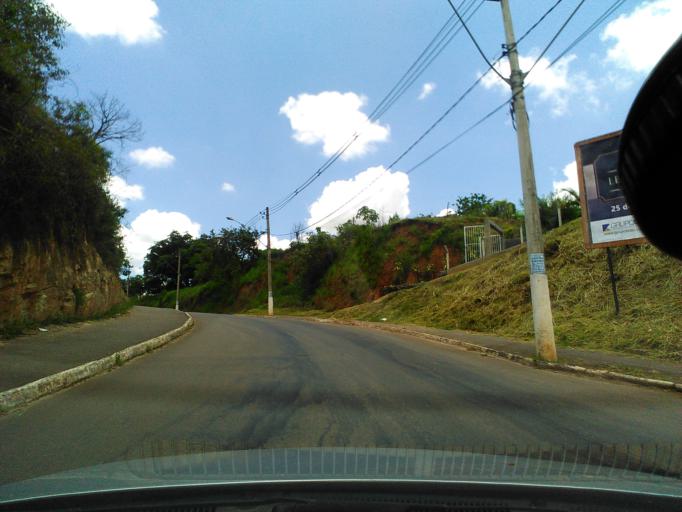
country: BR
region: Minas Gerais
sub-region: Tres Coracoes
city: Tres Coracoes
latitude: -21.7096
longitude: -45.2620
